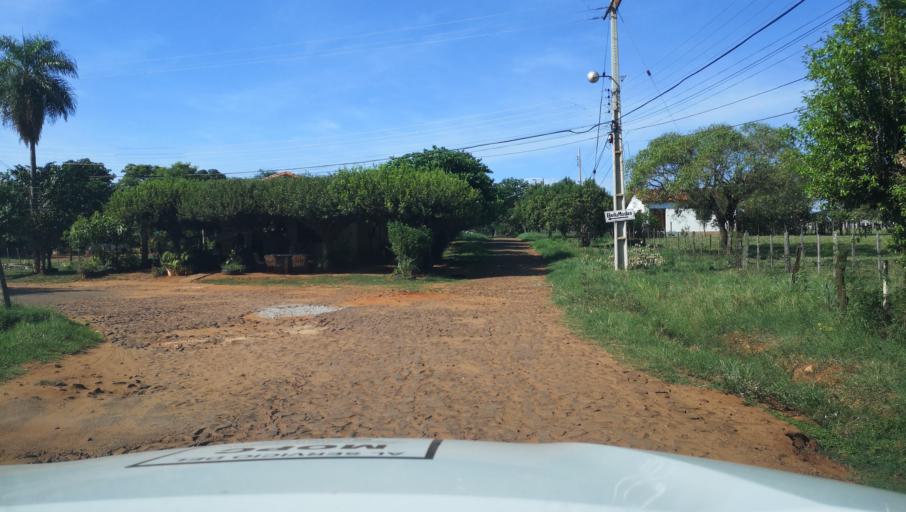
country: PY
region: Misiones
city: Santa Maria
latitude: -26.8949
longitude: -57.0182
